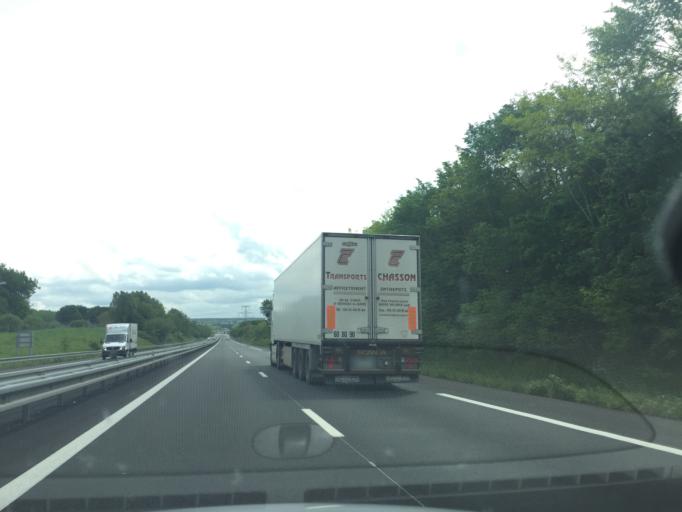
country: FR
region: Pays de la Loire
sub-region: Departement de la Sarthe
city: Ecommoy
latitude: 47.8334
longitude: 0.3059
